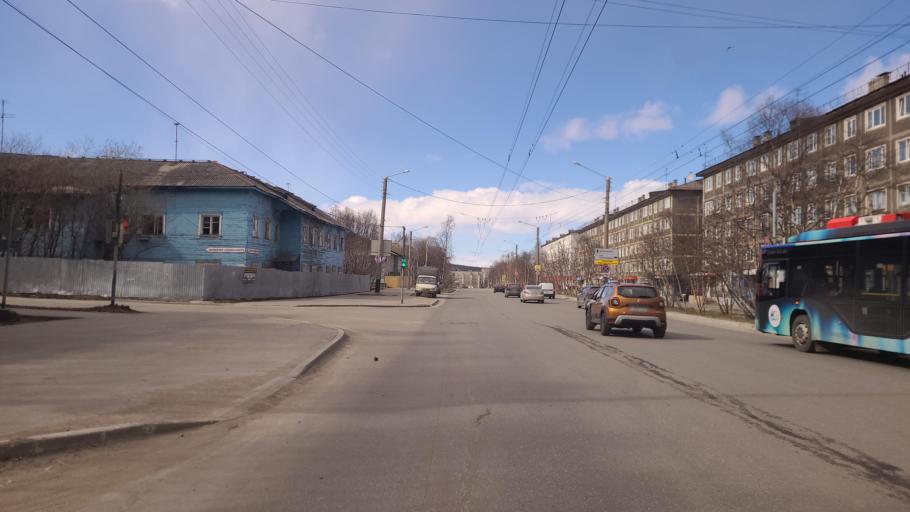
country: RU
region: Murmansk
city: Murmansk
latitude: 68.9520
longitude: 33.0731
